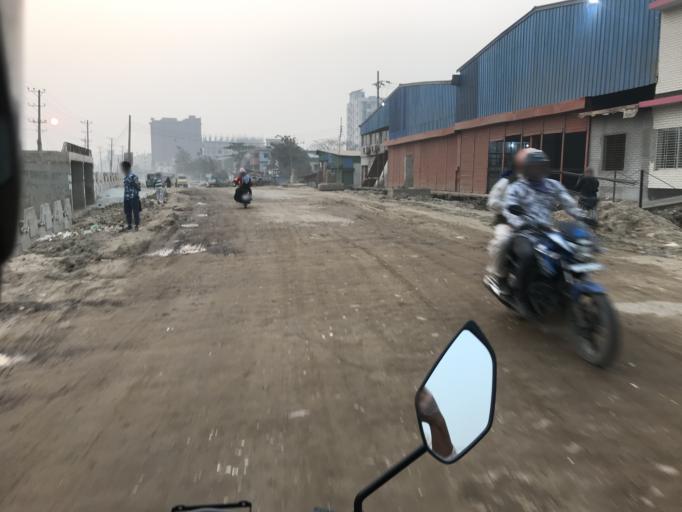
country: BD
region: Dhaka
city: Paltan
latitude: 23.7168
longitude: 90.4662
